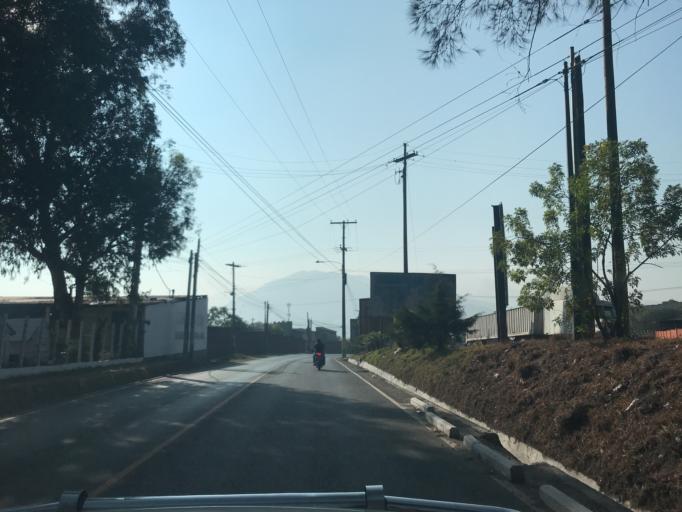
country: GT
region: Guatemala
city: Amatitlan
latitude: 14.4918
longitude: -90.6249
